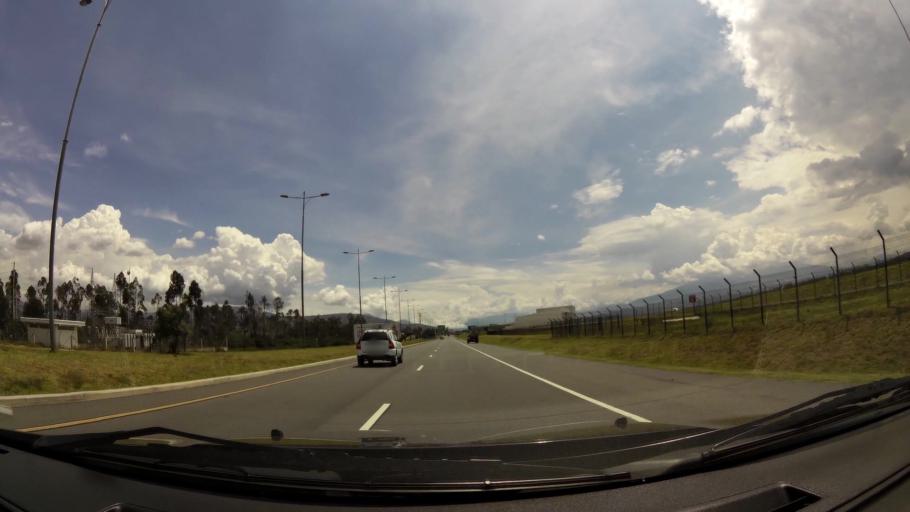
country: EC
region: Pichincha
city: Quito
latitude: -0.1425
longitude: -78.3562
